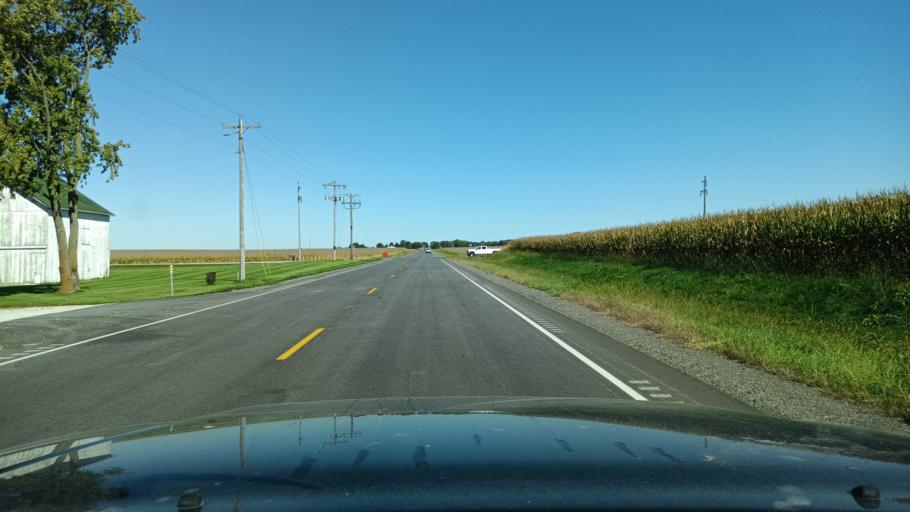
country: US
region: Illinois
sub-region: Champaign County
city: Philo
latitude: 39.9807
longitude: -88.1613
